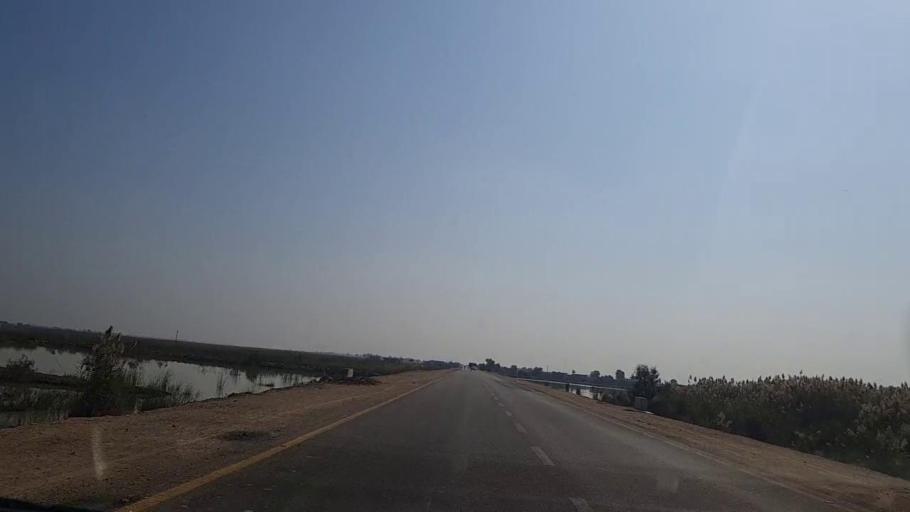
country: PK
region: Sindh
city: Sakrand
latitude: 26.0787
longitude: 68.4034
